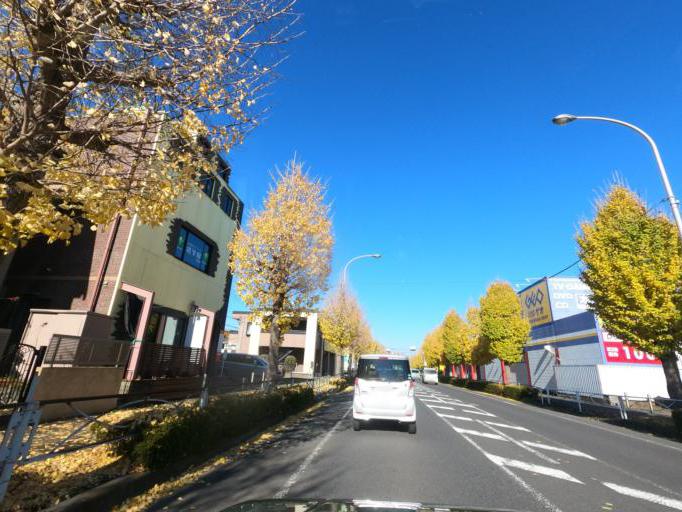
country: JP
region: Ibaraki
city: Mitsukaido
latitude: 35.9728
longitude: 139.9709
